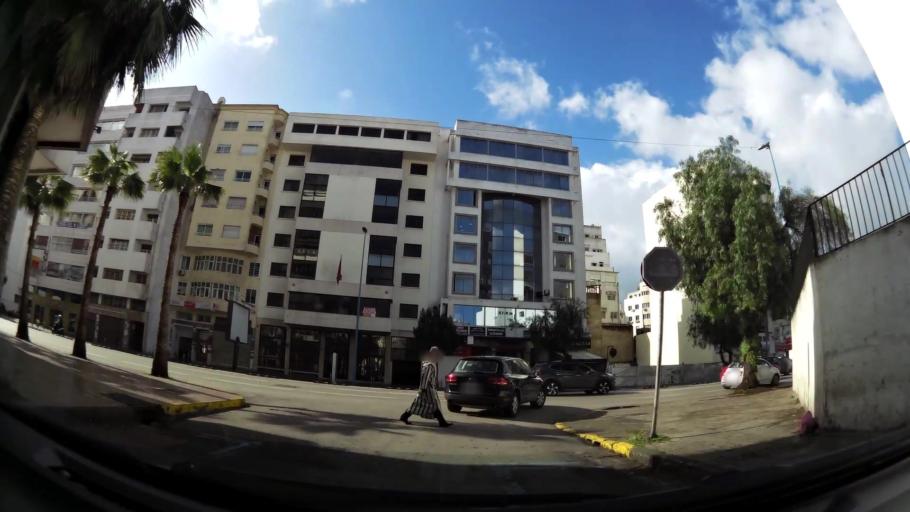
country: MA
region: Grand Casablanca
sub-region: Casablanca
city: Casablanca
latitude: 33.5835
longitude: -7.6142
